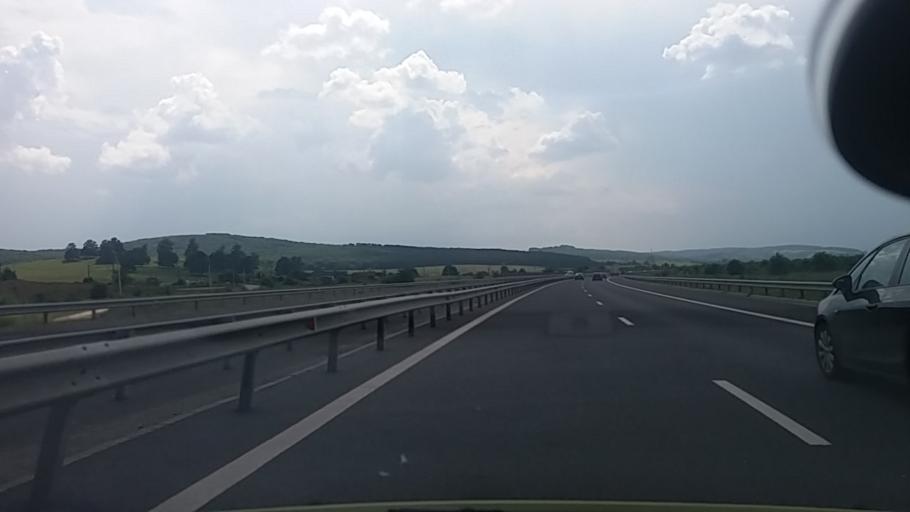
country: RO
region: Hunedoara
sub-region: Comuna Turdas
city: Turdas
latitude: 45.8391
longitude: 23.1187
